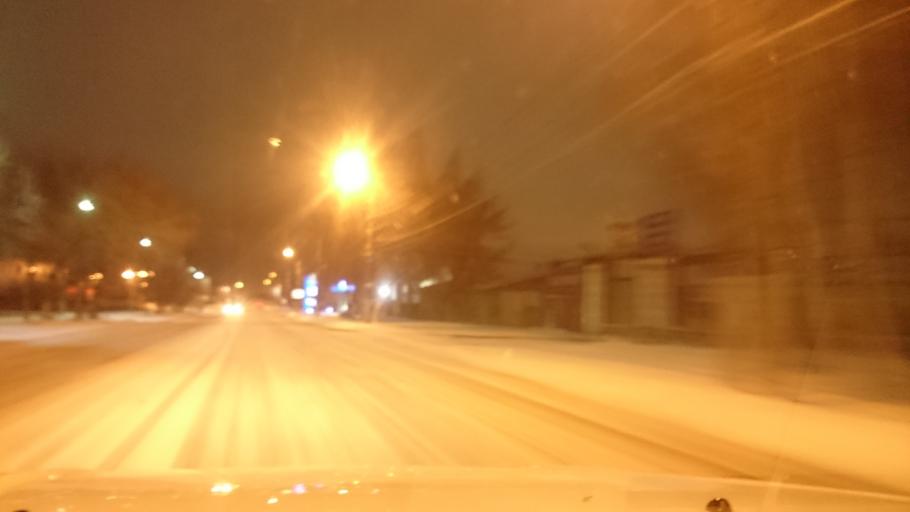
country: RU
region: Tula
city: Mendeleyevskiy
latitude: 54.1924
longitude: 37.5417
